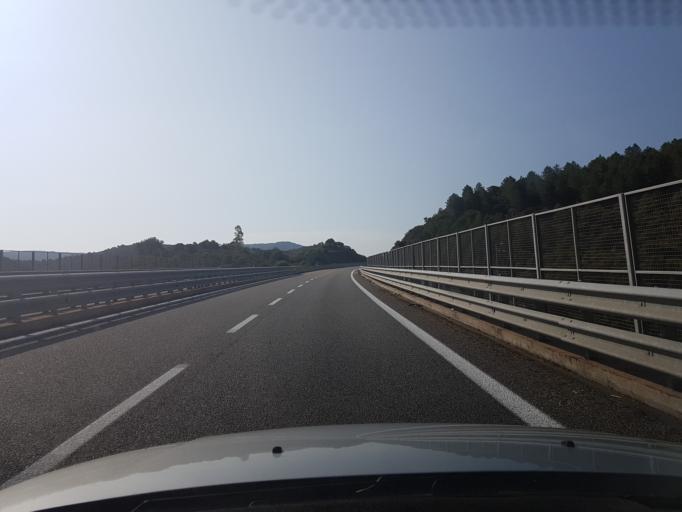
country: IT
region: Sardinia
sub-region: Provincia di Olbia-Tempio
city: Loiri Porto San Paolo
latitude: 40.8264
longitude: 9.5780
